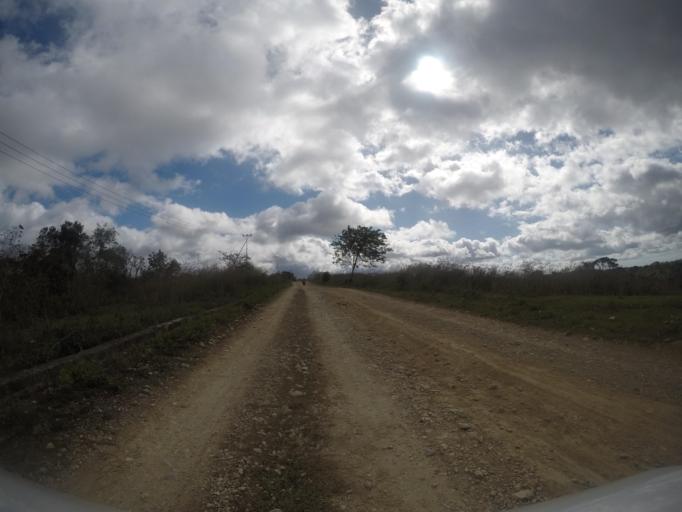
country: TL
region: Lautem
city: Lospalos
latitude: -8.5617
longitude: 126.8933
